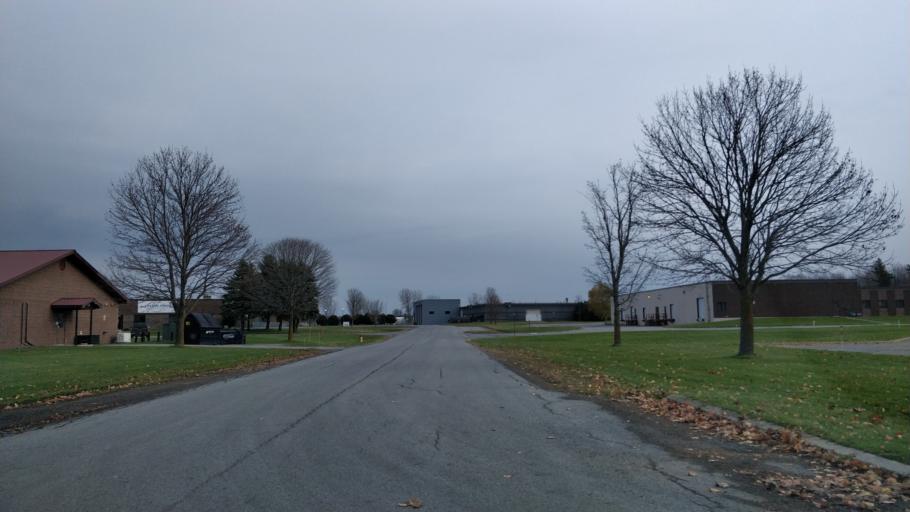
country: US
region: New York
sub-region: St. Lawrence County
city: Ogdensburg
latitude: 44.7177
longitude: -75.4496
